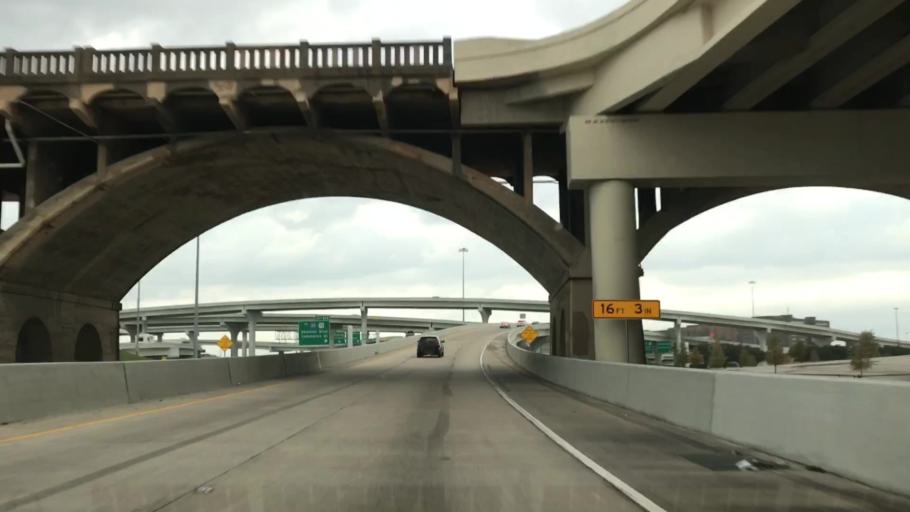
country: US
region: Texas
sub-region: Dallas County
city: Dallas
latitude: 32.7706
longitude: -96.8080
